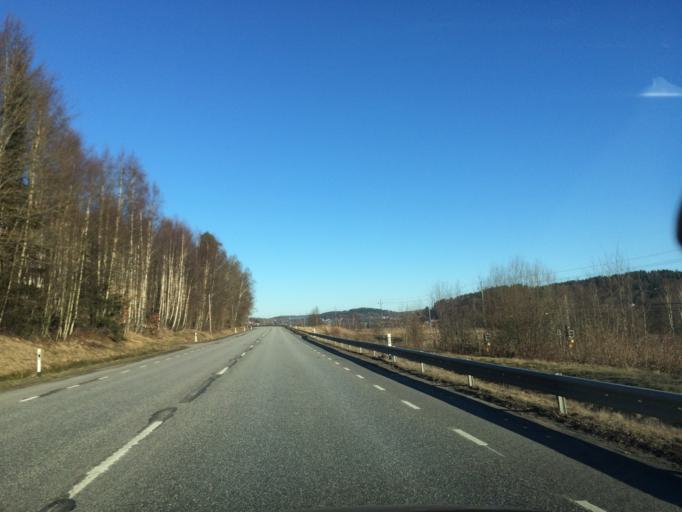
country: SE
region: Vaestra Goetaland
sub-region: Molndal
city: Lindome
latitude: 57.5498
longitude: 12.0944
